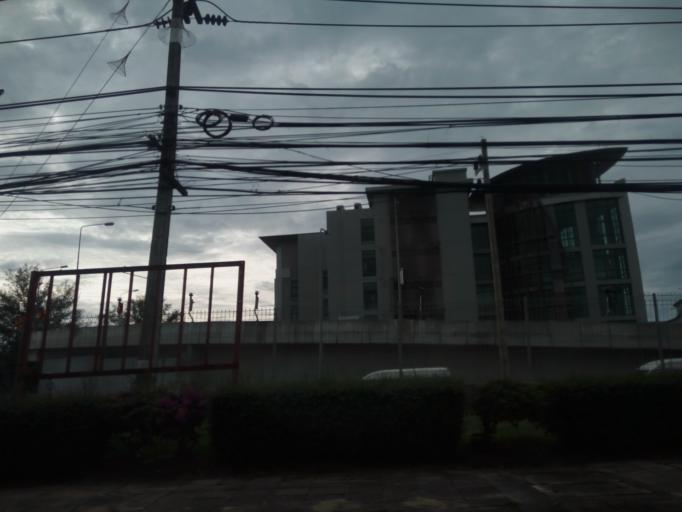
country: TH
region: Phuket
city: Thalang
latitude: 8.1031
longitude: 98.3072
